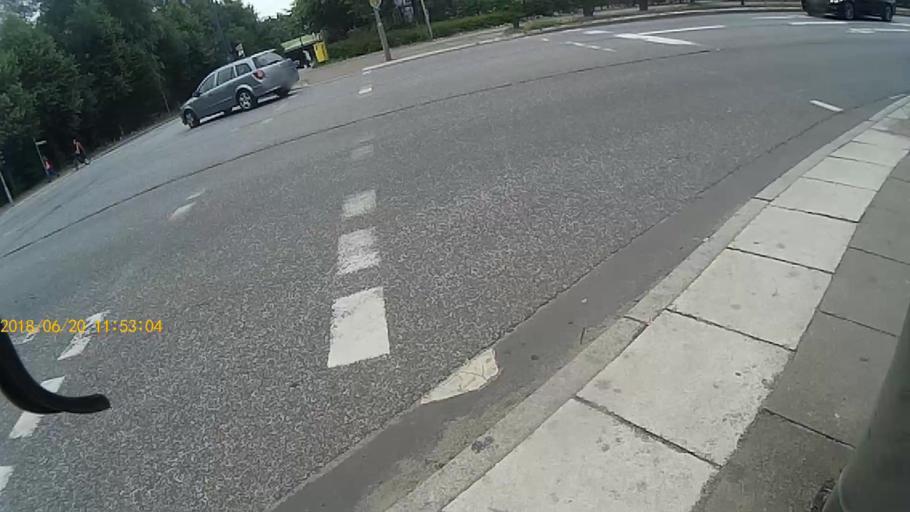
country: DE
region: Hamburg
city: Rothenburgsort
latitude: 53.5188
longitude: 10.0192
